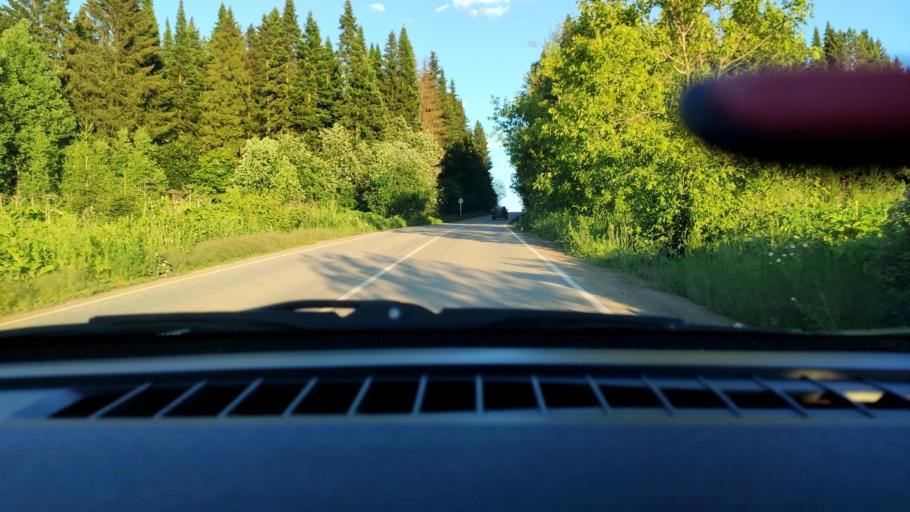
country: RU
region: Perm
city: Kultayevo
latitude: 57.9210
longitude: 55.9268
